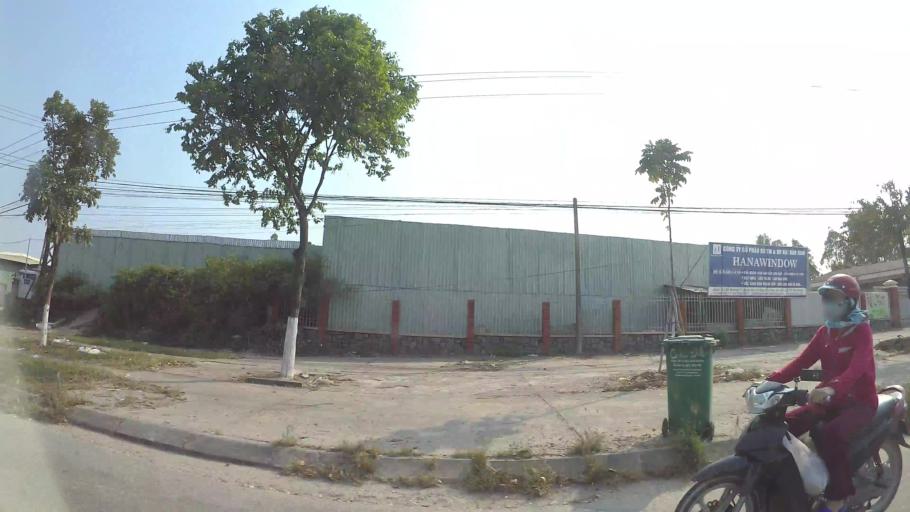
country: VN
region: Da Nang
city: Cam Le
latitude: 16.0124
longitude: 108.1828
